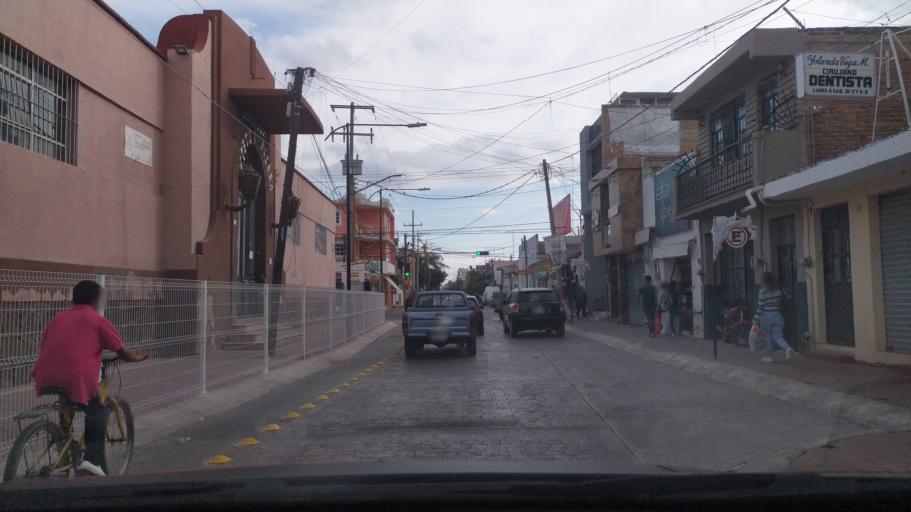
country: MX
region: Guanajuato
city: San Francisco del Rincon
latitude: 21.0162
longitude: -101.8568
